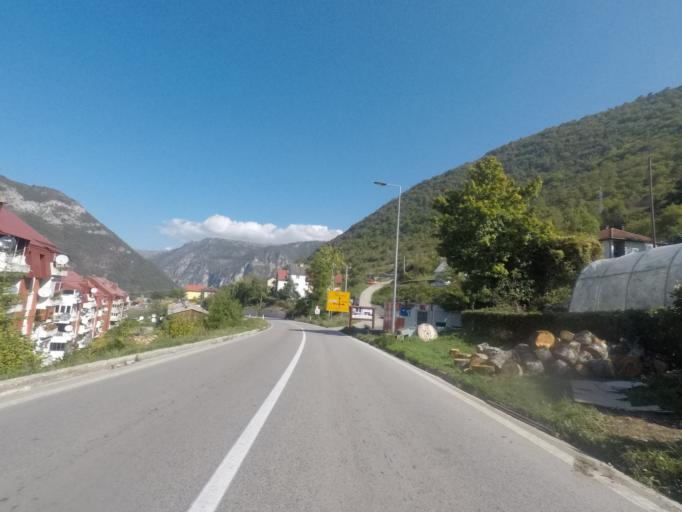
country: ME
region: Opstina Pluzine
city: Pluzine
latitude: 43.1546
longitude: 18.8461
